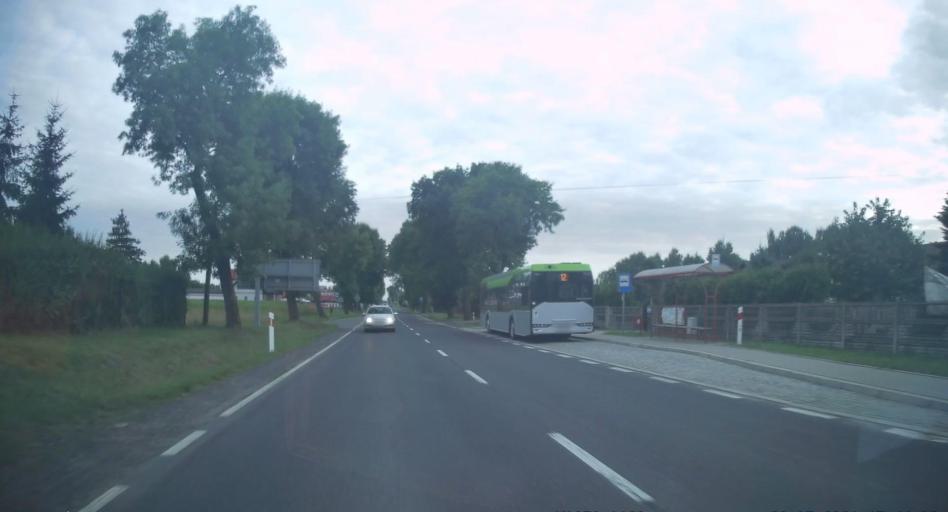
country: PL
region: Lodz Voivodeship
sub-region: Powiat radomszczanski
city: Radomsko
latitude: 51.1062
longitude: 19.4651
